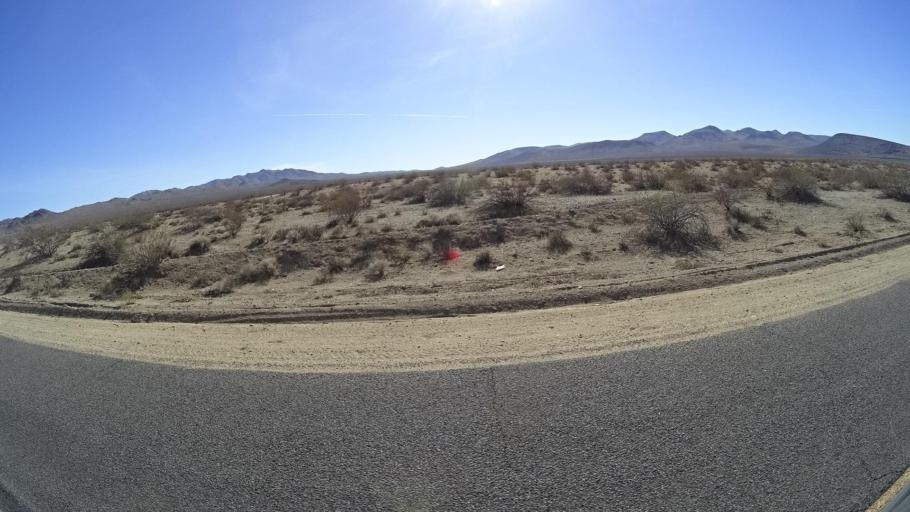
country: US
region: California
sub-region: Kern County
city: Ridgecrest
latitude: 35.5523
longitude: -117.7275
